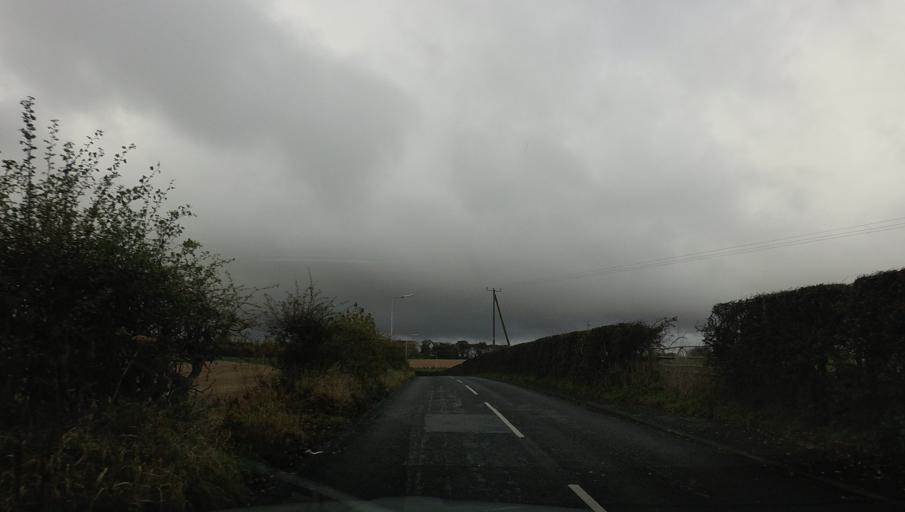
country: GB
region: Scotland
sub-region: Fife
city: East Wemyss
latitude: 56.1439
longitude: -3.0941
